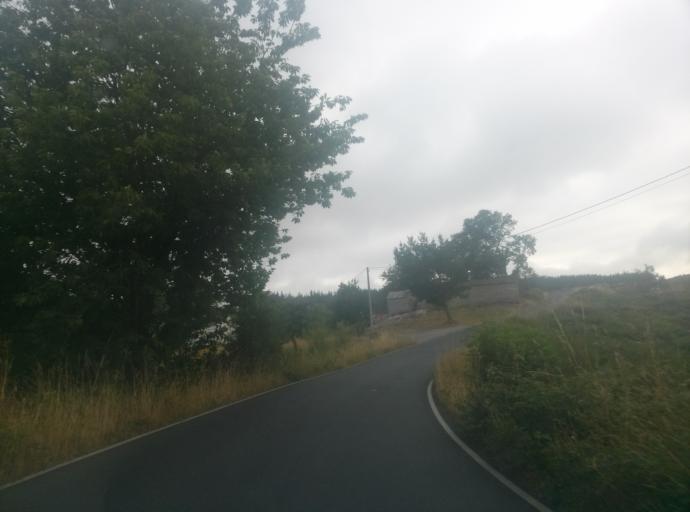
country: ES
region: Galicia
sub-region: Provincia de Lugo
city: Lugo
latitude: 43.0805
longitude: -7.5470
